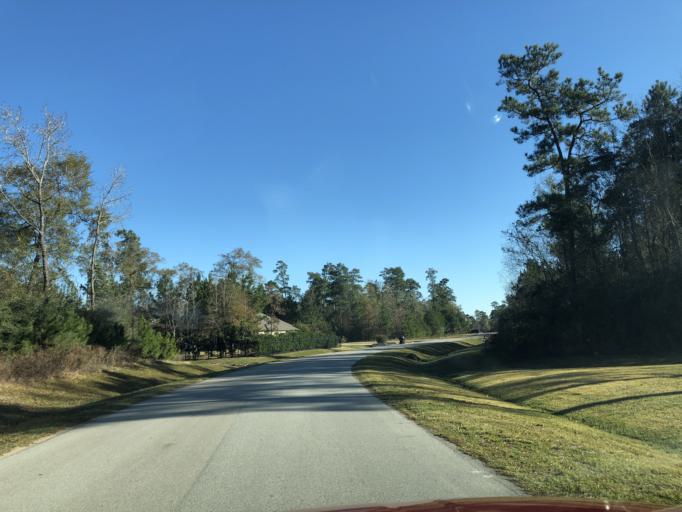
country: US
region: Texas
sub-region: Montgomery County
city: Porter Heights
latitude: 30.0818
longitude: -95.3352
